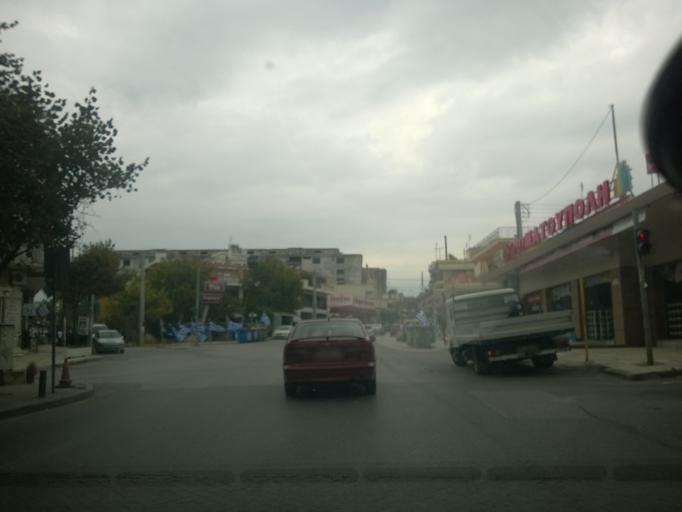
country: GR
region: Central Macedonia
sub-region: Nomos Thessalonikis
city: Stavroupoli
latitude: 40.6729
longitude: 22.9341
